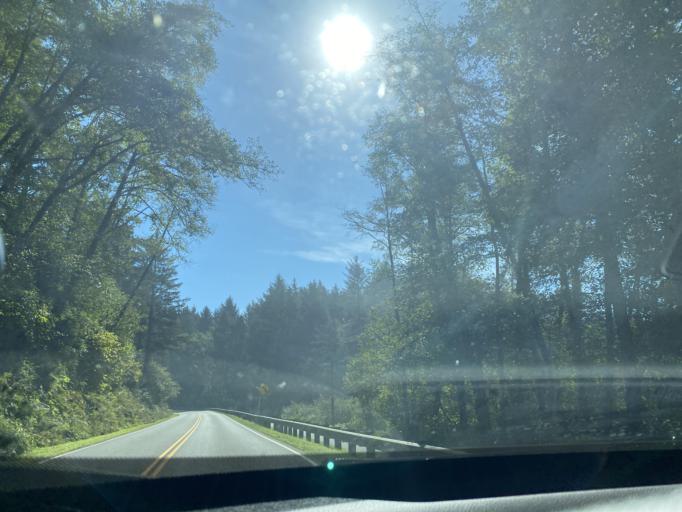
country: US
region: Washington
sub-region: Clallam County
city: Forks
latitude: 47.9002
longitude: -124.6263
